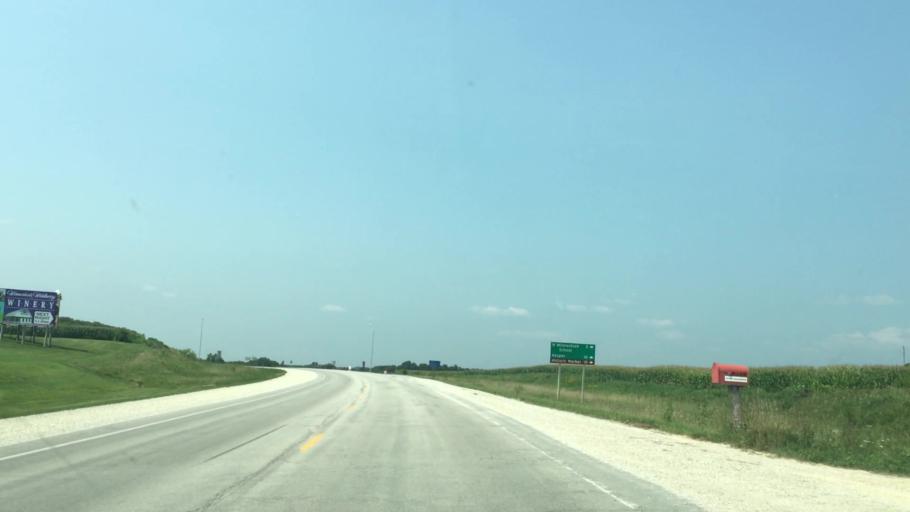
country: US
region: Iowa
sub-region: Winneshiek County
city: Decorah
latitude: 43.3655
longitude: -91.8049
